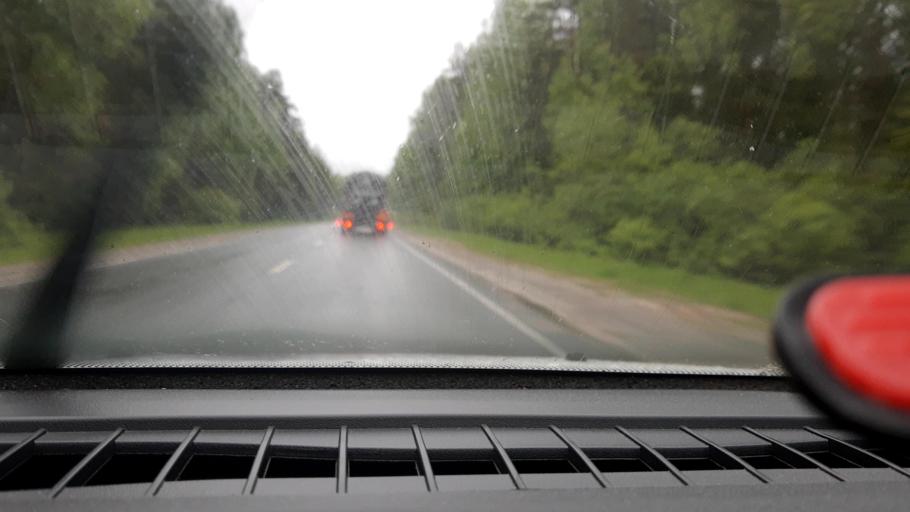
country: RU
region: Nizjnij Novgorod
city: Vladimirskoye
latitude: 56.9070
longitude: 45.0301
